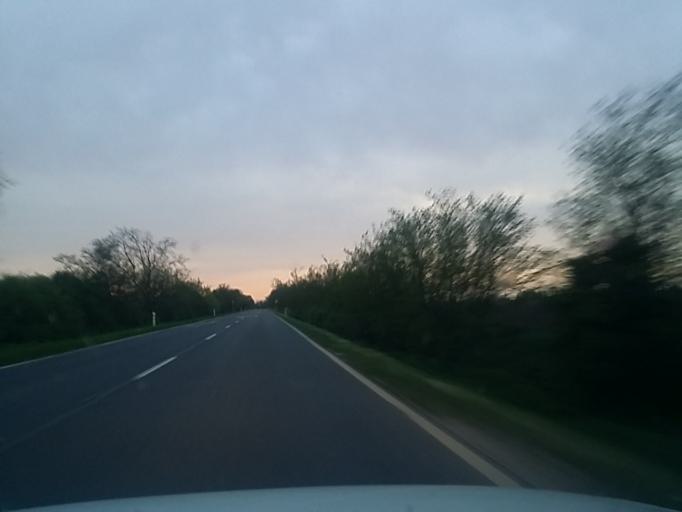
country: HU
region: Bekes
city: Csorvas
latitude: 46.7219
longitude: 20.9274
